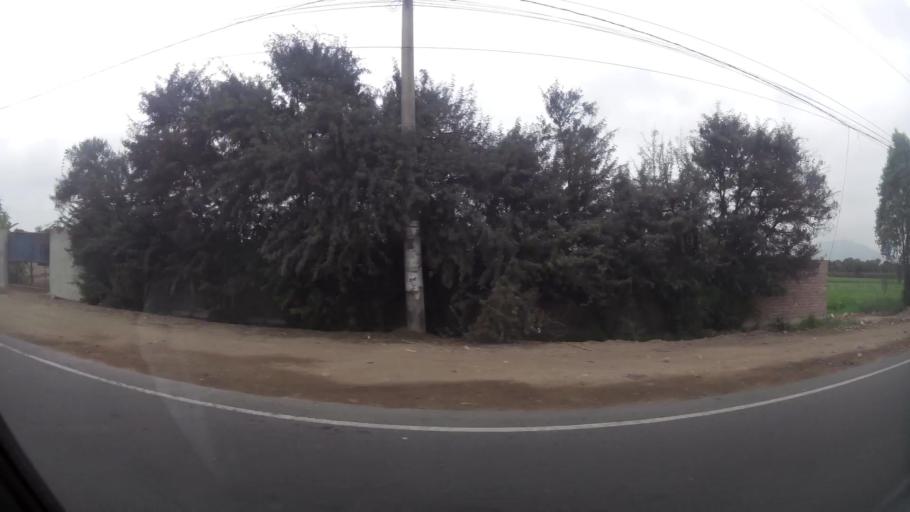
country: PE
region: Lima
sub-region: Provincia de Huaral
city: Huaral
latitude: -11.5147
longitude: -77.2360
